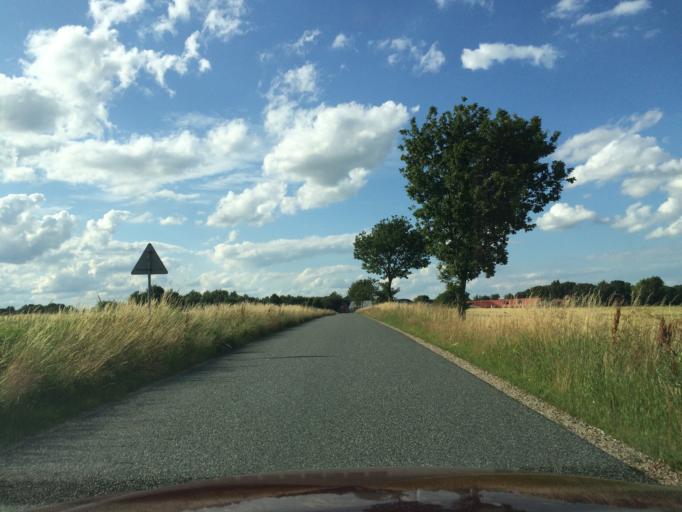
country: DK
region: Central Jutland
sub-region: Viborg Kommune
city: Bjerringbro
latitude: 56.2494
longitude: 9.7122
